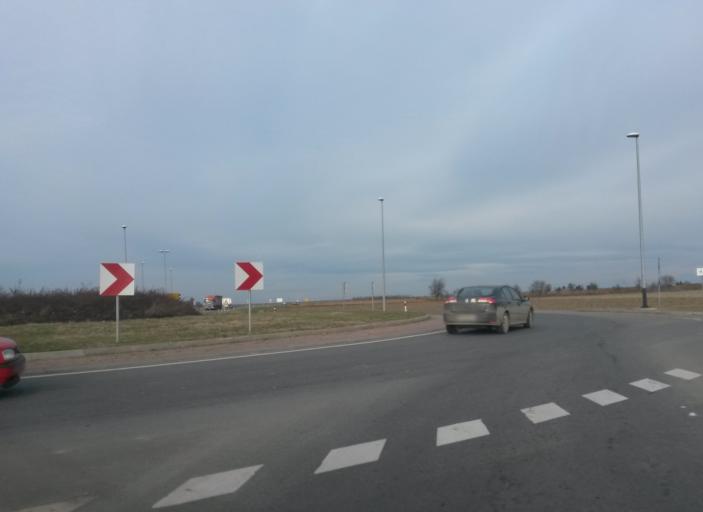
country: HR
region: Osjecko-Baranjska
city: Cepin
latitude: 45.5155
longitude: 18.5372
